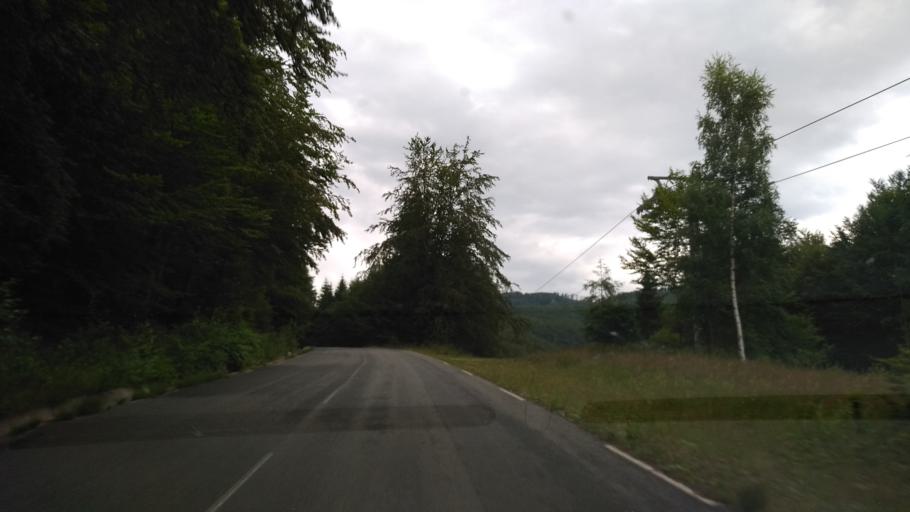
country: RO
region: Hunedoara
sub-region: Municipiul  Vulcan
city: Jiu-Paroseni
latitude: 45.3443
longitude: 23.2908
